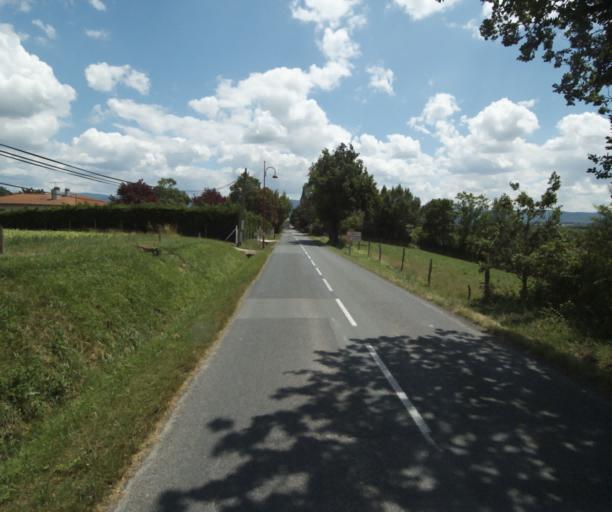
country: FR
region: Midi-Pyrenees
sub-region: Departement du Tarn
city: Soual
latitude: 43.5308
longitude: 2.0623
